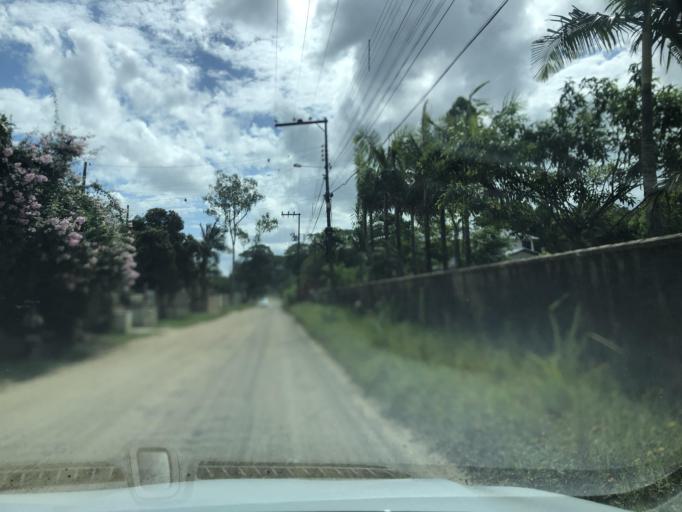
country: BR
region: Santa Catarina
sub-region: Sao Francisco Do Sul
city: Sao Francisco do Sul
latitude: -26.2275
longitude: -48.5840
